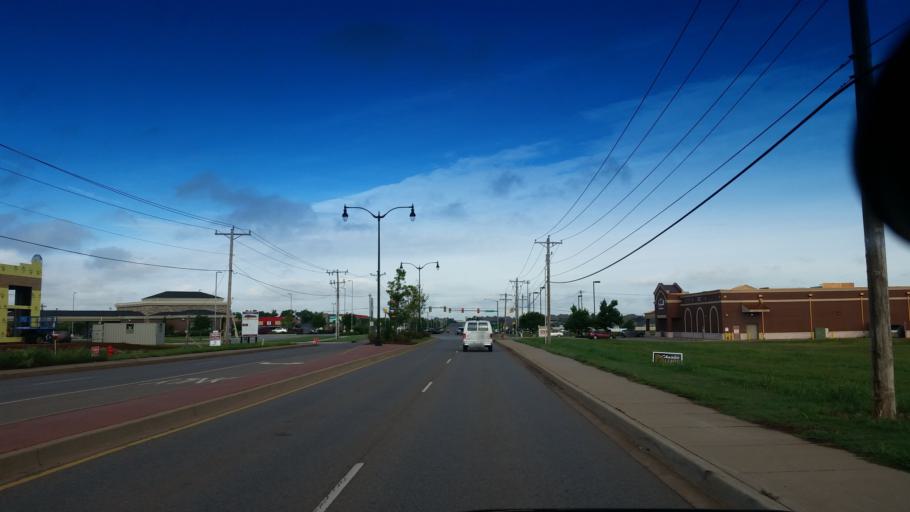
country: US
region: Oklahoma
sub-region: Oklahoma County
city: Edmond
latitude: 35.6238
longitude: -97.5115
